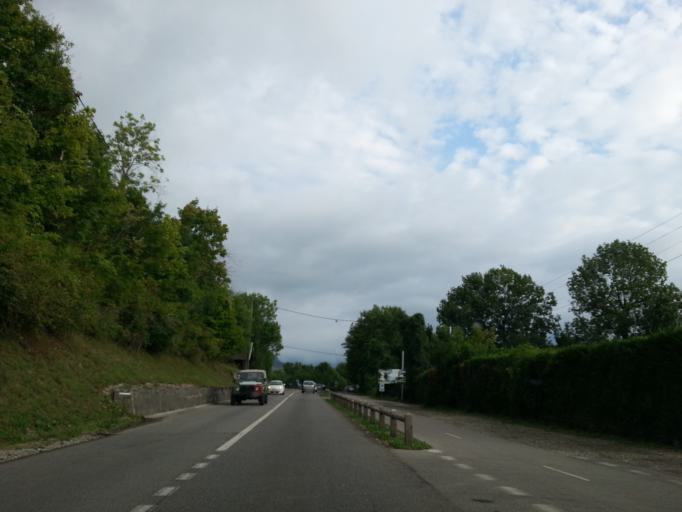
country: FR
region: Rhone-Alpes
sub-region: Departement de la Haute-Savoie
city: Talloires
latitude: 45.8310
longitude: 6.2203
